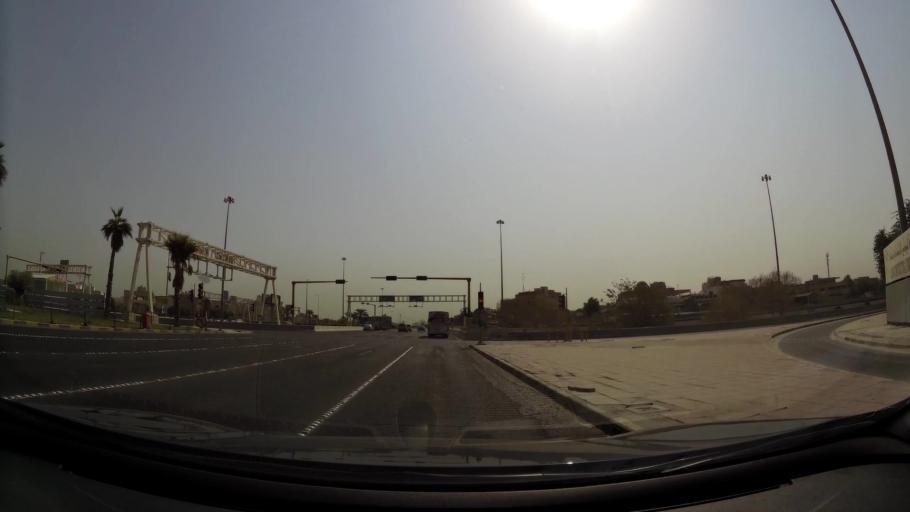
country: KW
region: Al Asimah
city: Ad Dasmah
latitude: 29.3651
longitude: 47.9913
